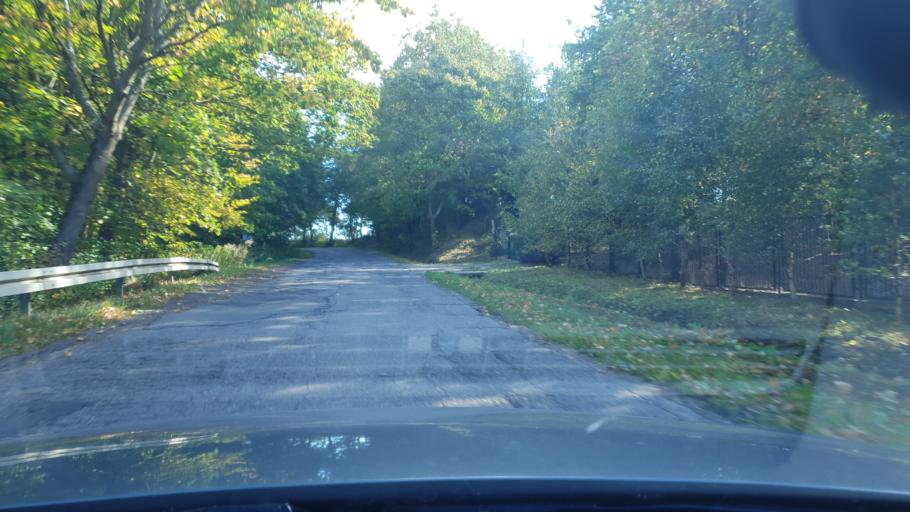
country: PL
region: Pomeranian Voivodeship
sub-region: Powiat pucki
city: Zelistrzewo
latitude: 54.6891
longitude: 18.4259
